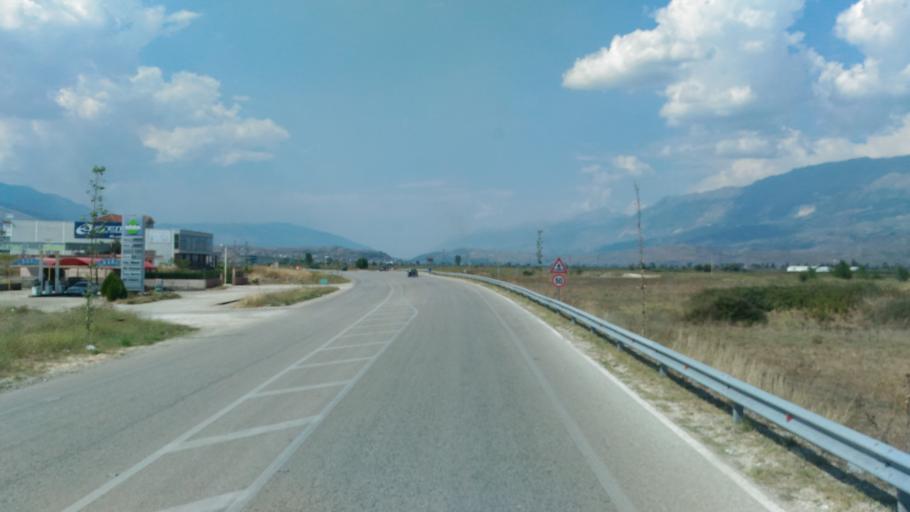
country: AL
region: Gjirokaster
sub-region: Rrethi i Gjirokastres
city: Dervician
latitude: 40.0195
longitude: 20.1946
